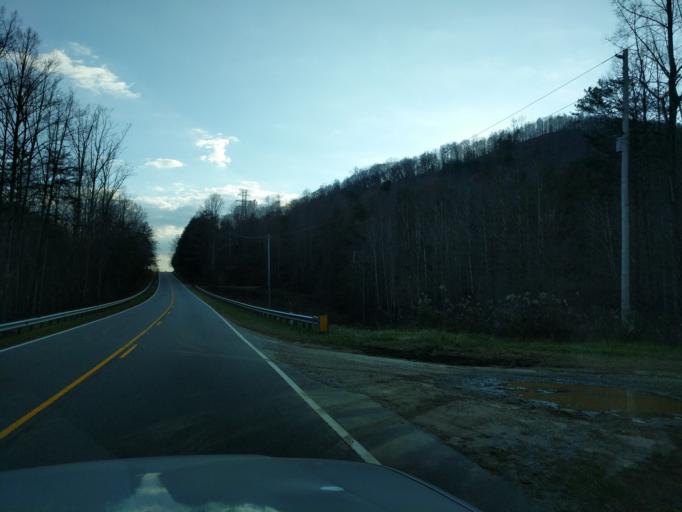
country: US
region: North Carolina
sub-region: McDowell County
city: West Marion
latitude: 35.5412
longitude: -81.9640
